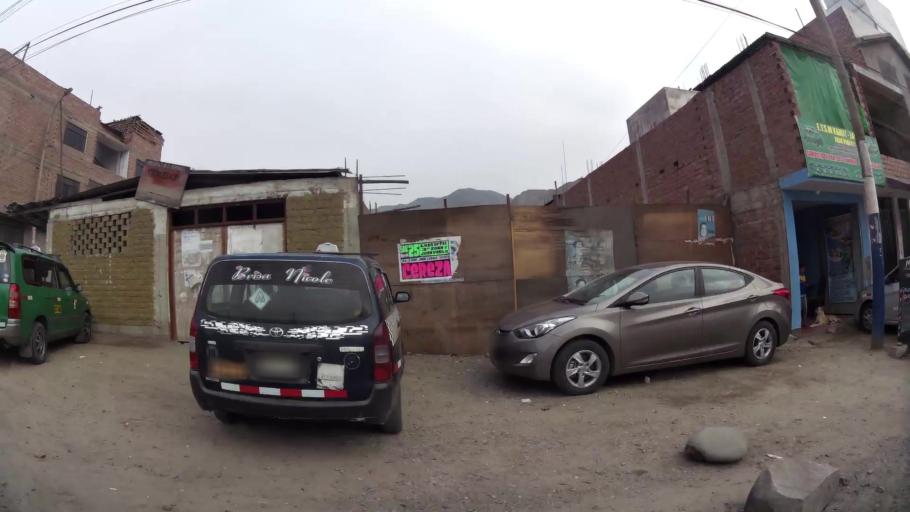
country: PE
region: Lima
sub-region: Lima
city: Independencia
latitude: -11.9811
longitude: -76.9843
